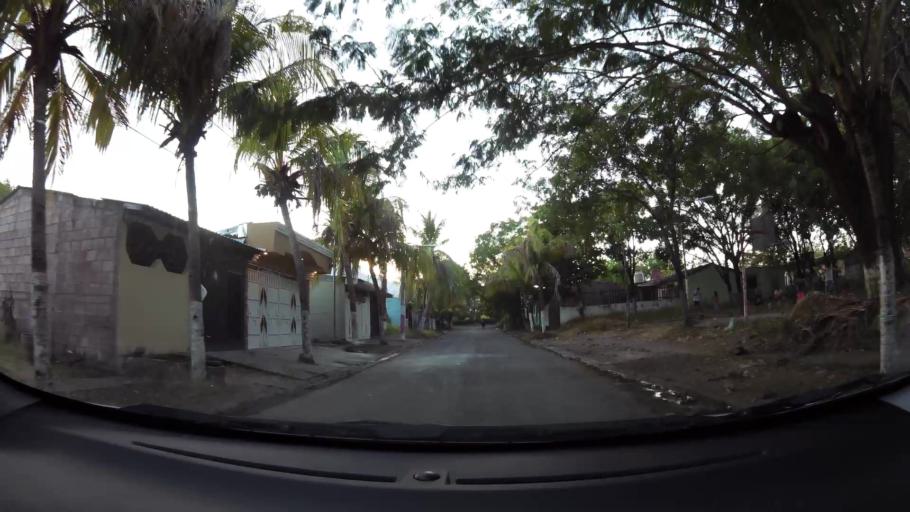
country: SV
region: San Miguel
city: San Miguel
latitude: 13.4791
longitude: -88.1569
